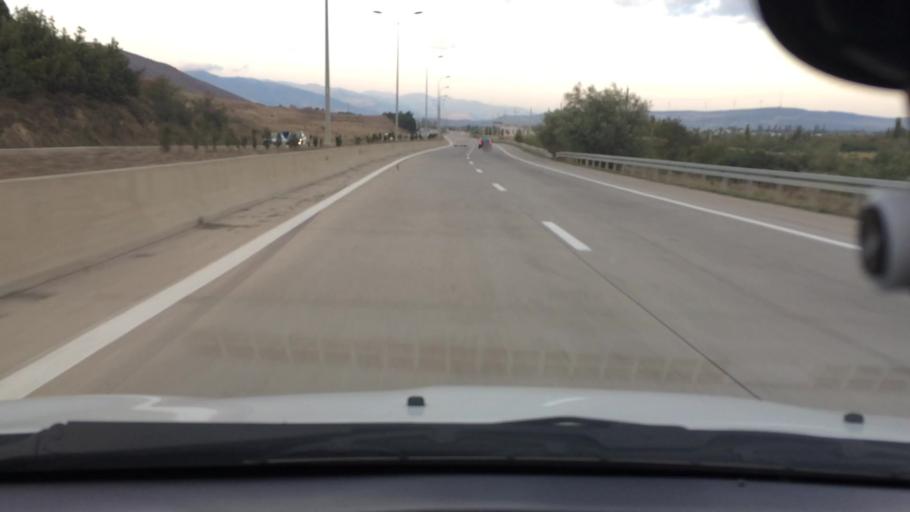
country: GE
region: Shida Kartli
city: Gori
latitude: 42.0264
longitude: 44.1737
